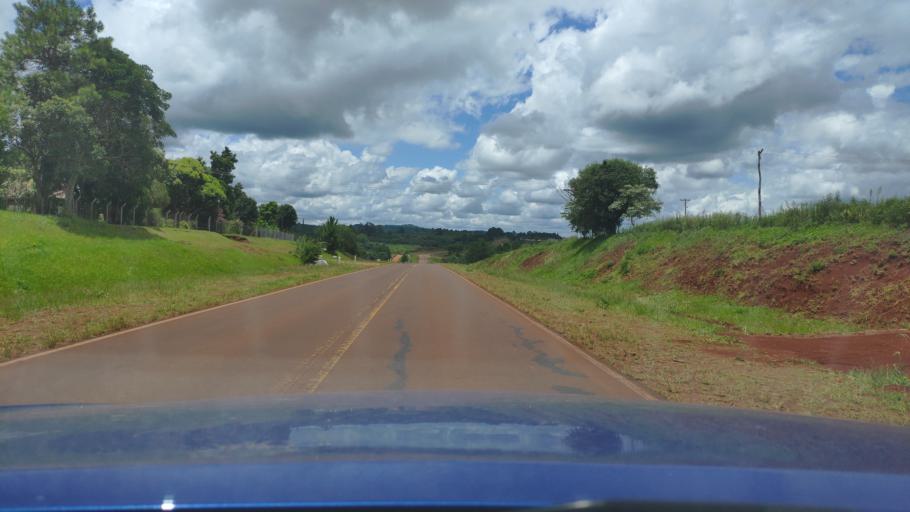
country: AR
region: Misiones
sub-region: Departamento de San Javier
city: San Javier
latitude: -27.8420
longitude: -55.2372
